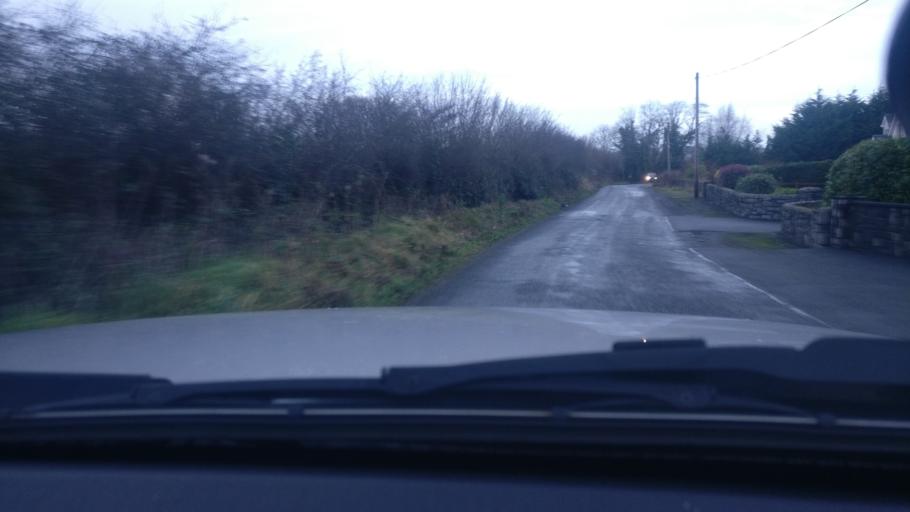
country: IE
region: Connaught
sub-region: County Galway
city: Loughrea
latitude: 53.1625
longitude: -8.5056
